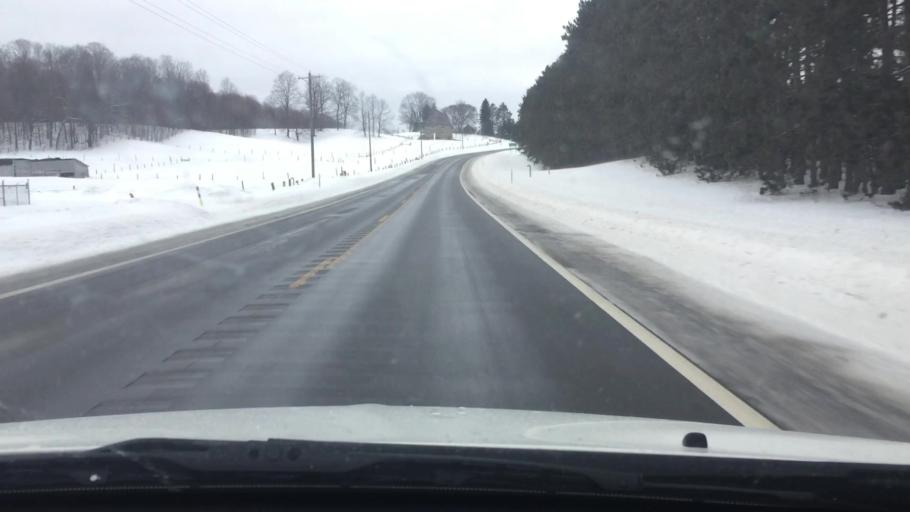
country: US
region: Michigan
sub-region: Charlevoix County
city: Boyne City
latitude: 45.0946
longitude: -84.9731
